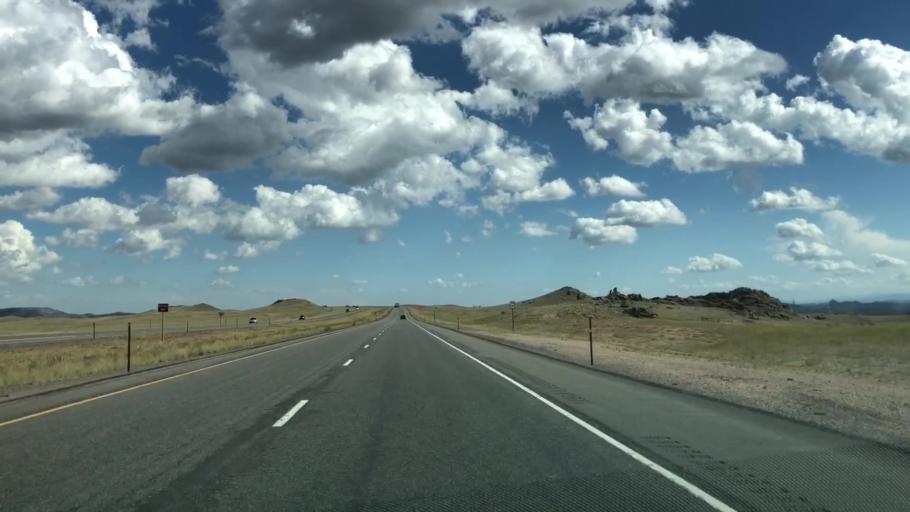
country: US
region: Wyoming
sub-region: Albany County
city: Laramie
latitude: 41.0507
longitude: -105.4679
